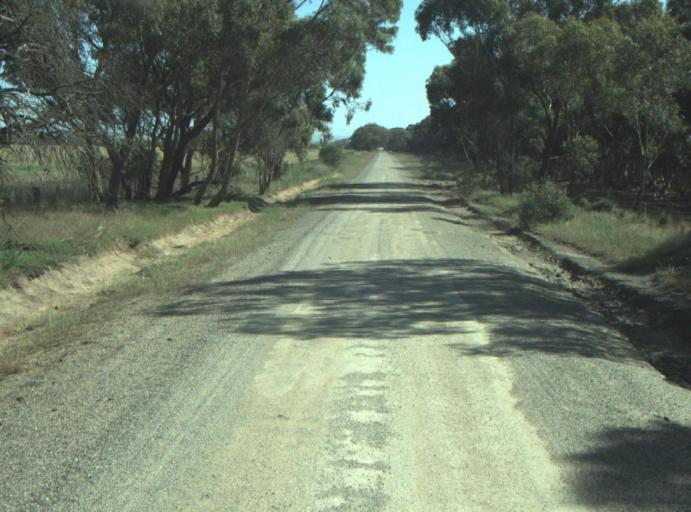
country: AU
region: Victoria
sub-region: Wyndham
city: Little River
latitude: -37.8924
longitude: 144.4019
